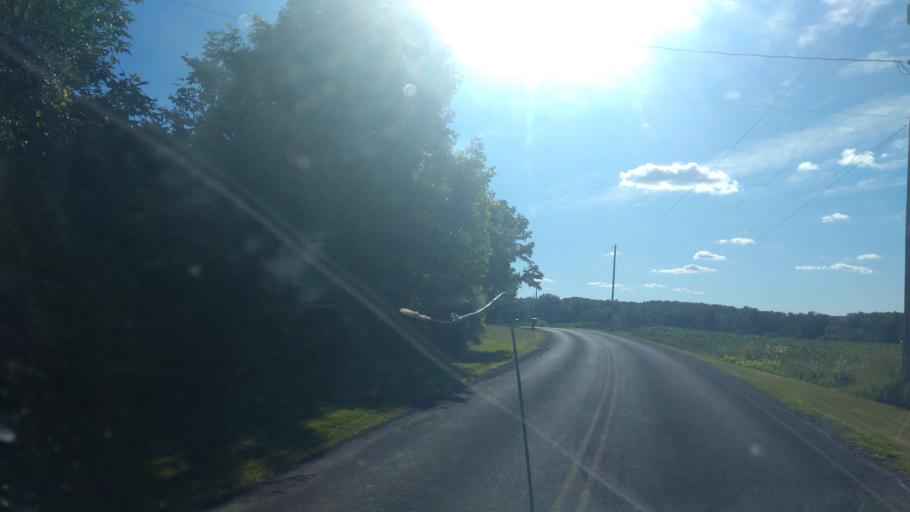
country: US
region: New York
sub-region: Wayne County
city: Lyons
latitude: 43.0118
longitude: -76.9805
